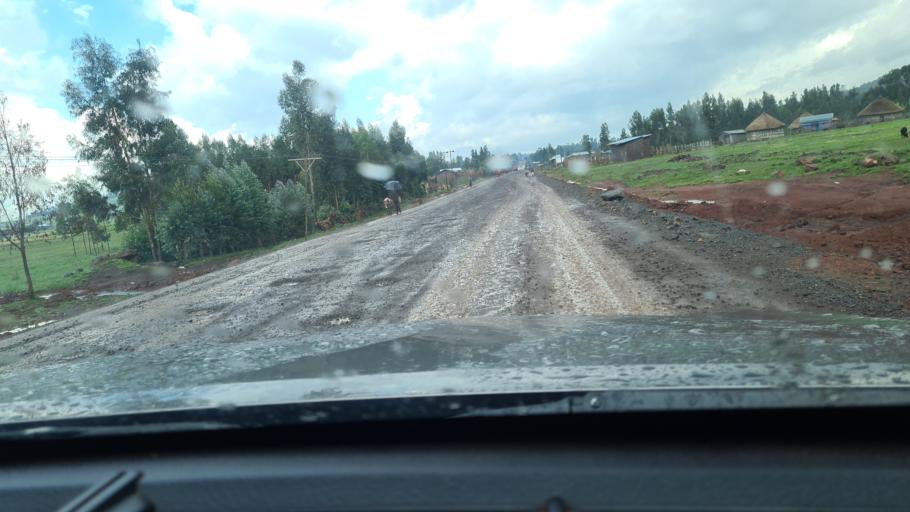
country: ET
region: Oromiya
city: Huruta
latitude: 8.0777
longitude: 39.5463
